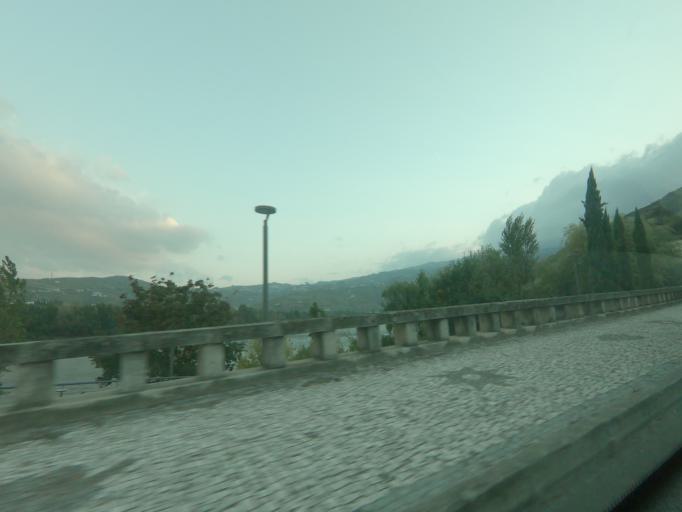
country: PT
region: Vila Real
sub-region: Peso da Regua
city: Godim
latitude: 41.1605
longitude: -7.8049
